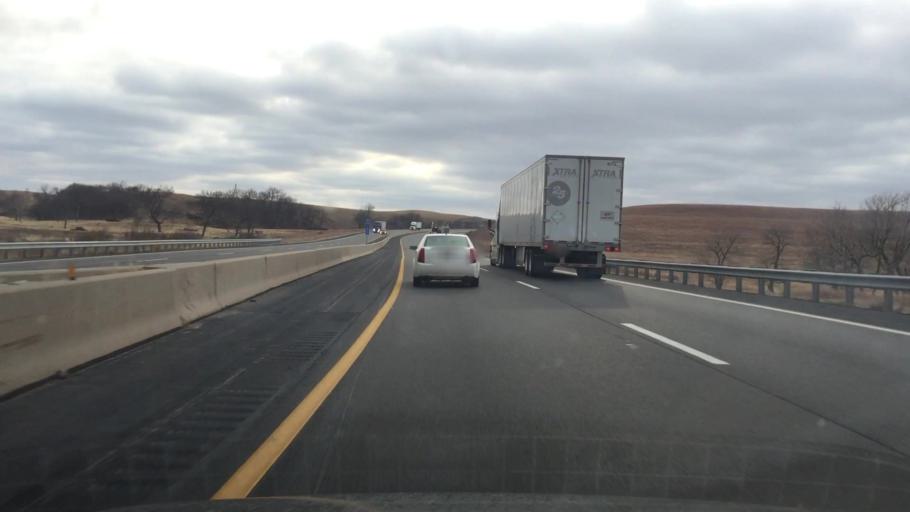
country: US
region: Kansas
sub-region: Chase County
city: Cottonwood Falls
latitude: 38.1722
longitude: -96.4740
